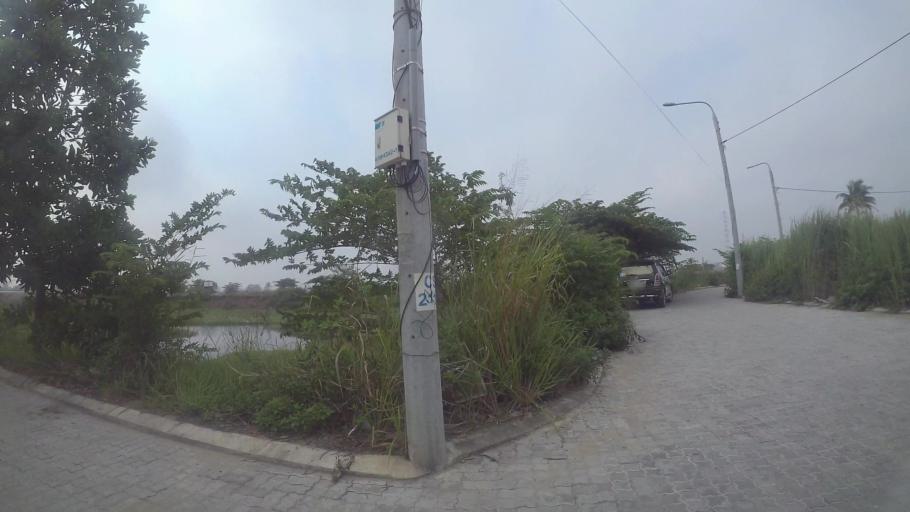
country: VN
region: Da Nang
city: Ngu Hanh Son
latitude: 16.0212
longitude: 108.2425
